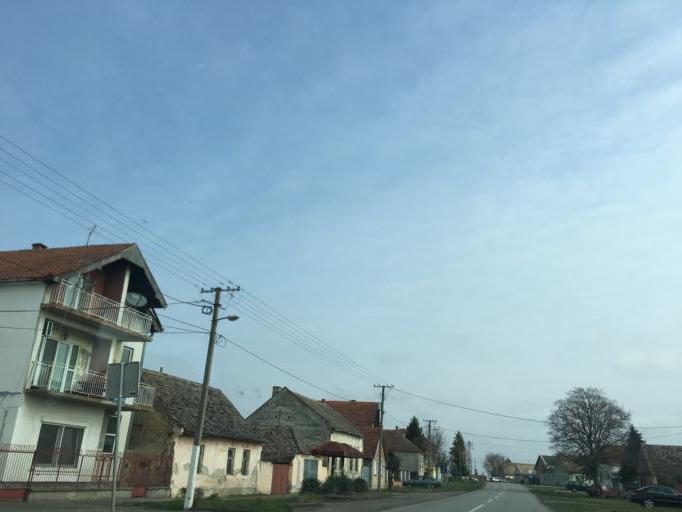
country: RS
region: Autonomna Pokrajina Vojvodina
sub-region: Juznobanatski Okrug
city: Opovo
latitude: 45.0566
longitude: 20.4295
